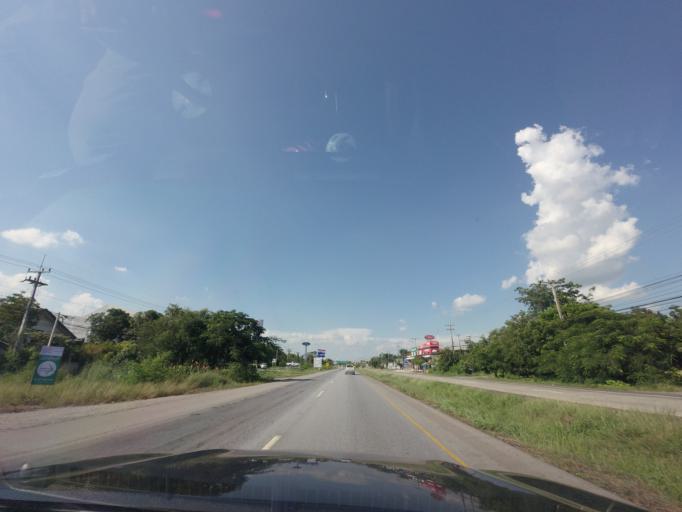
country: TH
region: Nakhon Ratchasima
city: Sida
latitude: 15.5420
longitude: 102.5467
